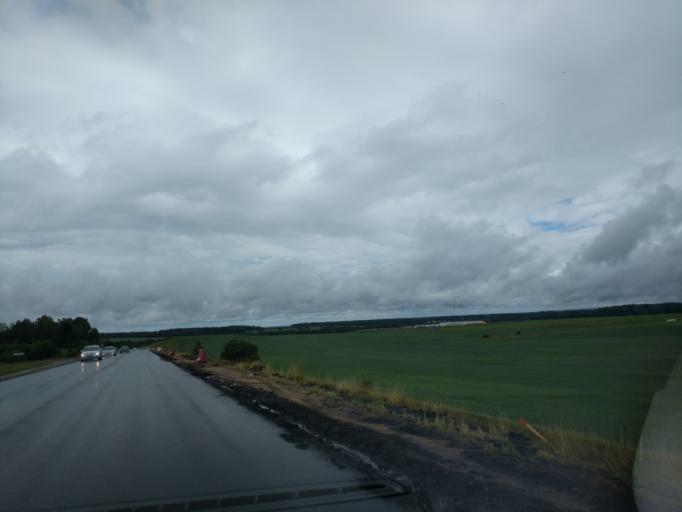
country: BY
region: Minsk
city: Il'ya
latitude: 54.2870
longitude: 27.4866
